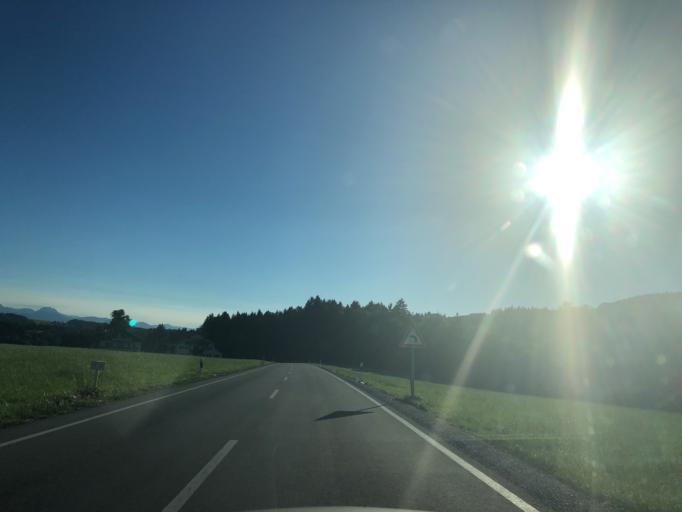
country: DE
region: Bavaria
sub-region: Upper Bavaria
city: Rimsting
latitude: 47.8629
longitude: 12.3077
